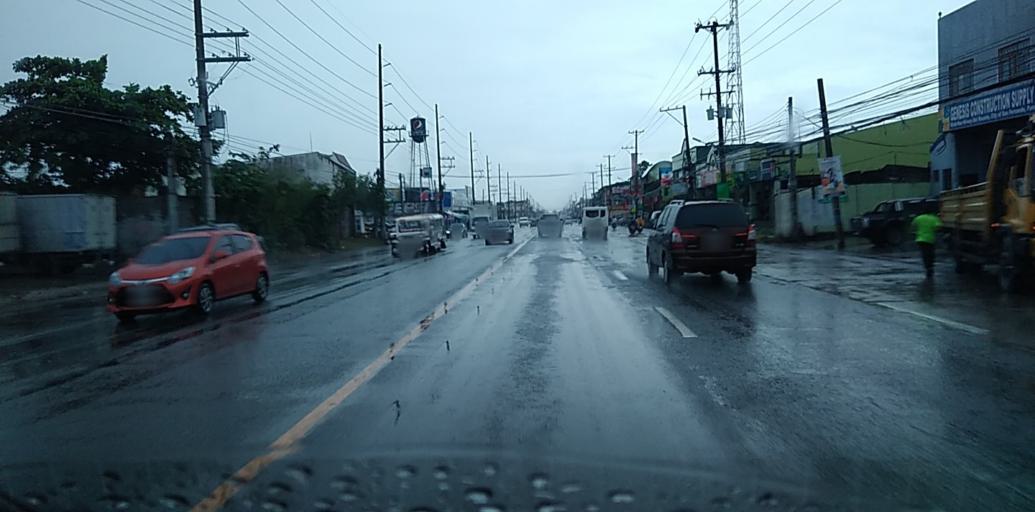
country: PH
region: Central Luzon
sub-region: Province of Pampanga
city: Bulaon
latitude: 15.0705
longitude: 120.6471
